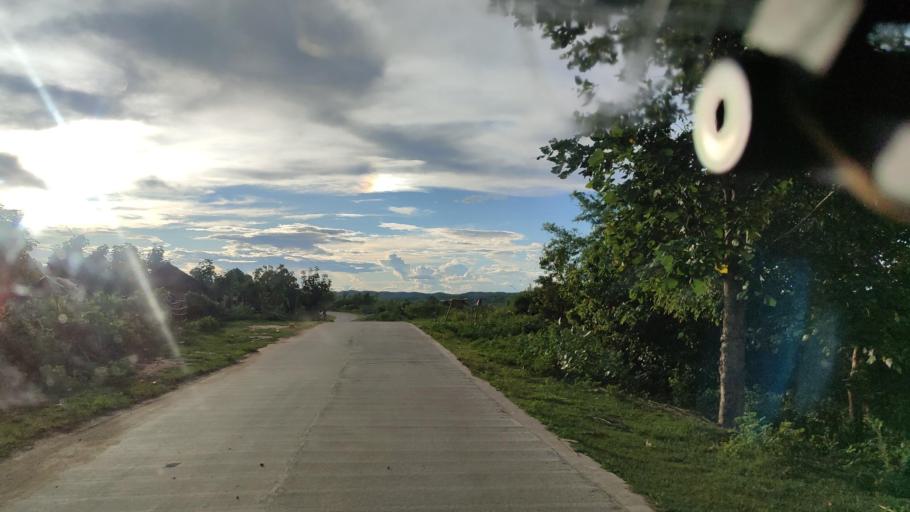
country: MM
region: Magway
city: Taungdwingyi
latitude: 20.0223
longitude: 95.8261
